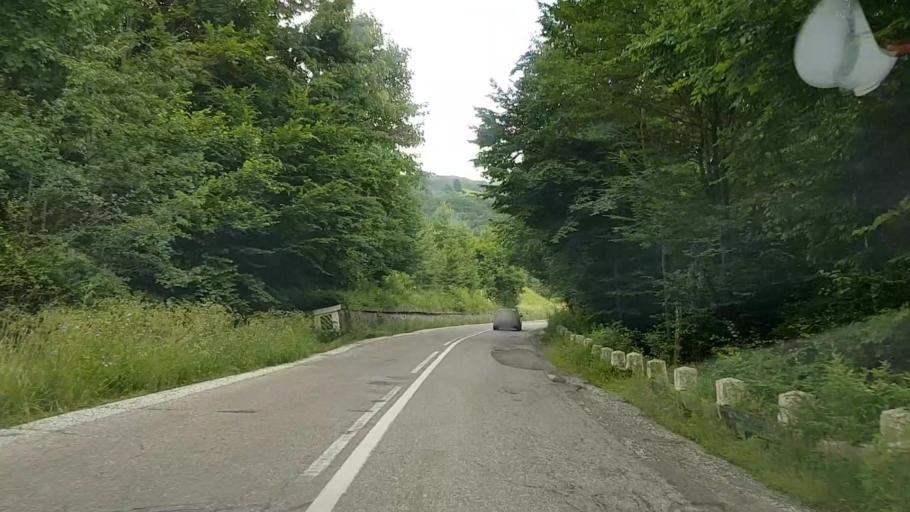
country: RO
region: Neamt
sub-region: Comuna Pangarati
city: Pangarati
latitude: 46.9521
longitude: 26.1258
